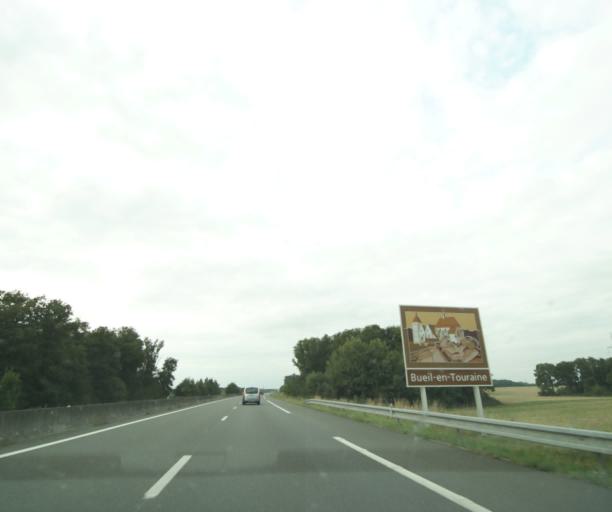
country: FR
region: Centre
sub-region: Departement d'Indre-et-Loire
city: Saint-Antoine-du-Rocher
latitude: 47.5051
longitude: 0.6394
